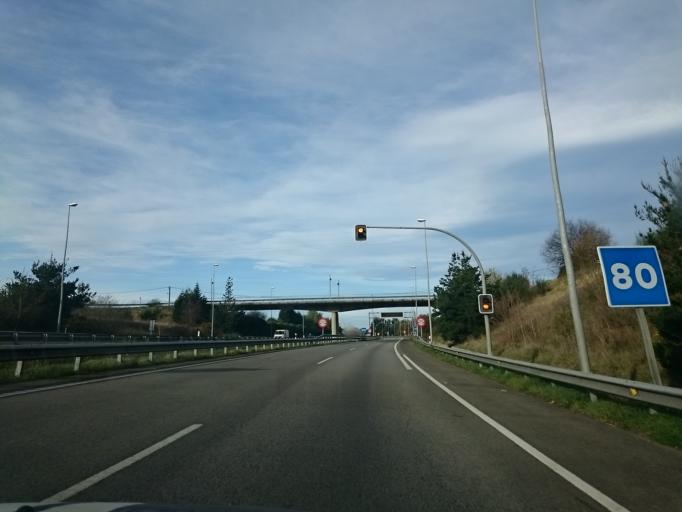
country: ES
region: Asturias
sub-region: Province of Asturias
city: Gijon
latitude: 43.5167
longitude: -5.6290
